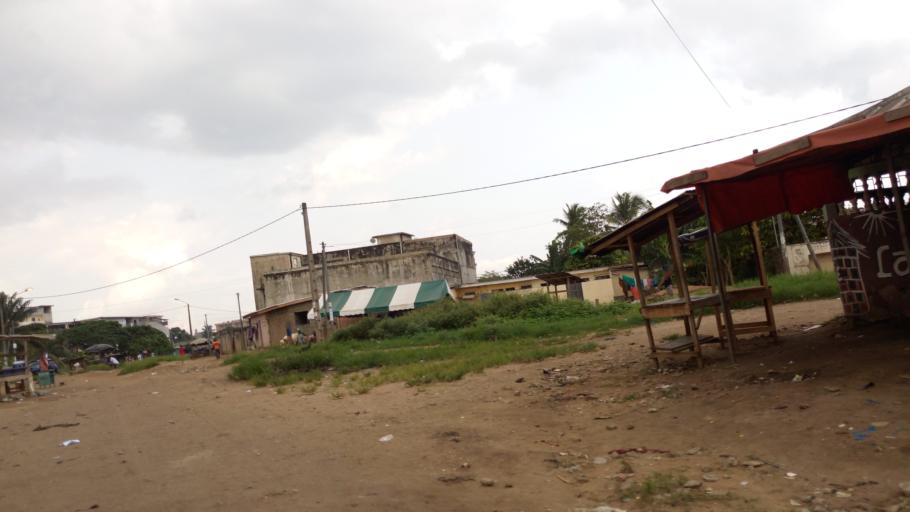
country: CI
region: Lagunes
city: Abobo
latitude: 5.4064
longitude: -3.9979
